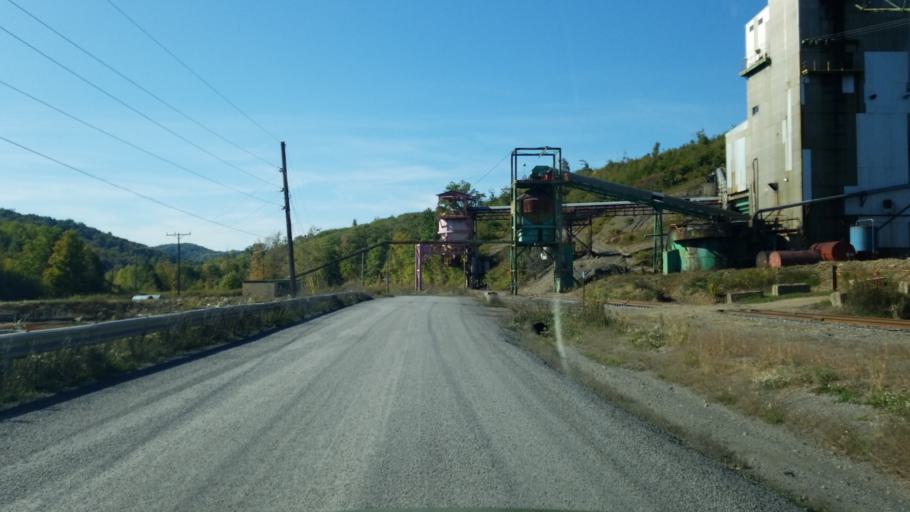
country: US
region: Pennsylvania
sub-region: Clearfield County
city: Treasure Lake
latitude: 41.1996
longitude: -78.5506
